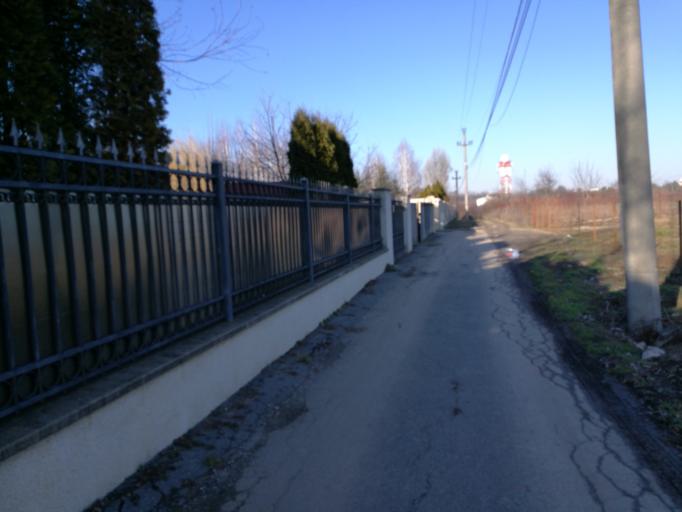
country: RO
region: Ilfov
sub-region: Comuna Otopeni
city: Otopeni
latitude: 44.5078
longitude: 26.0766
